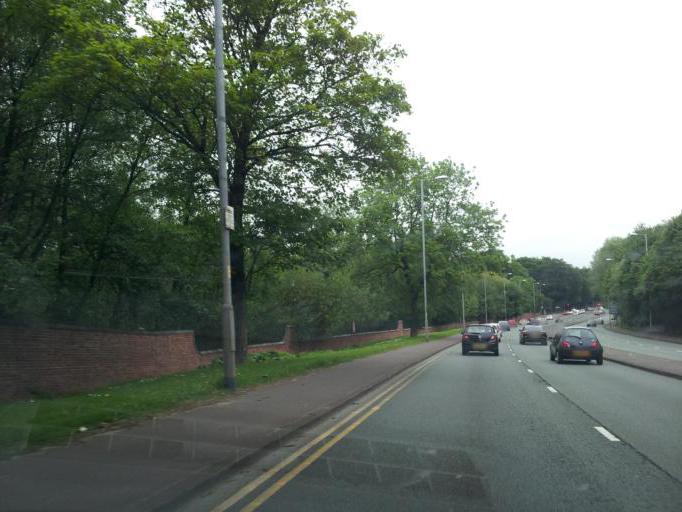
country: GB
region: England
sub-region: Manchester
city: Crumpsall
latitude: 53.5345
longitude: -2.2441
